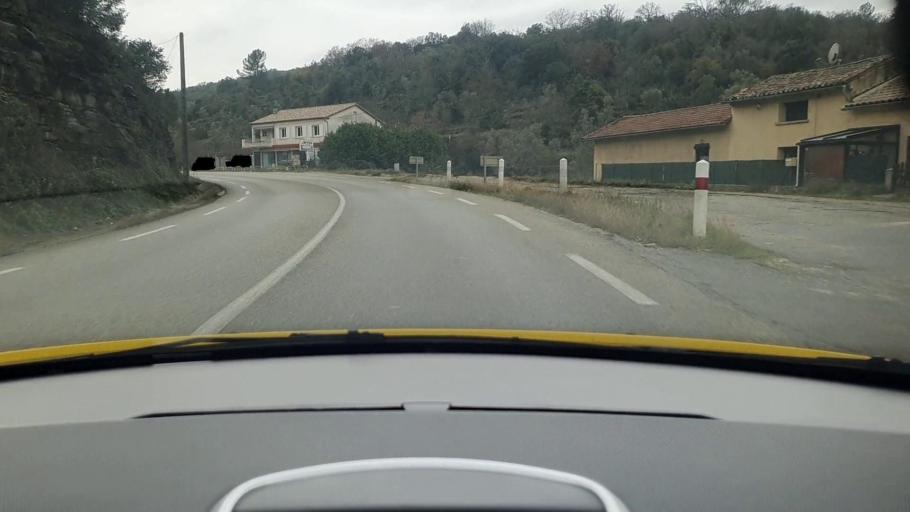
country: FR
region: Languedoc-Roussillon
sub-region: Departement du Gard
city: Rousson
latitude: 44.2107
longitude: 4.1456
